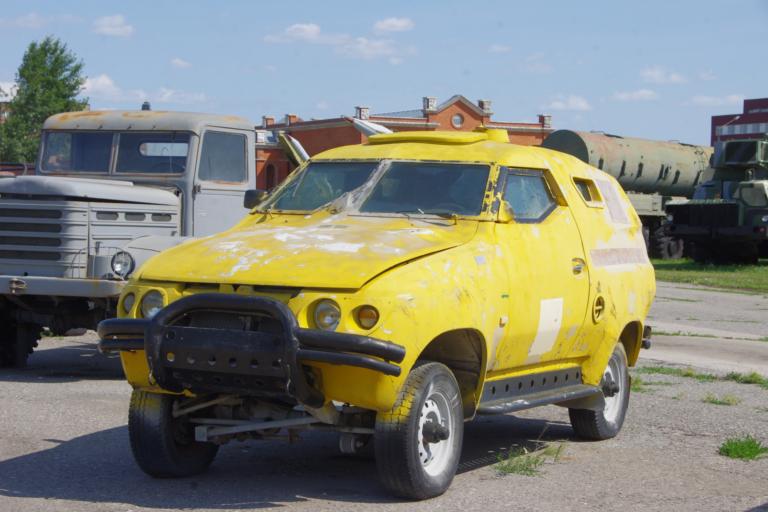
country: RU
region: Samara
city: Tol'yatti
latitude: 53.5525
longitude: 49.2555
